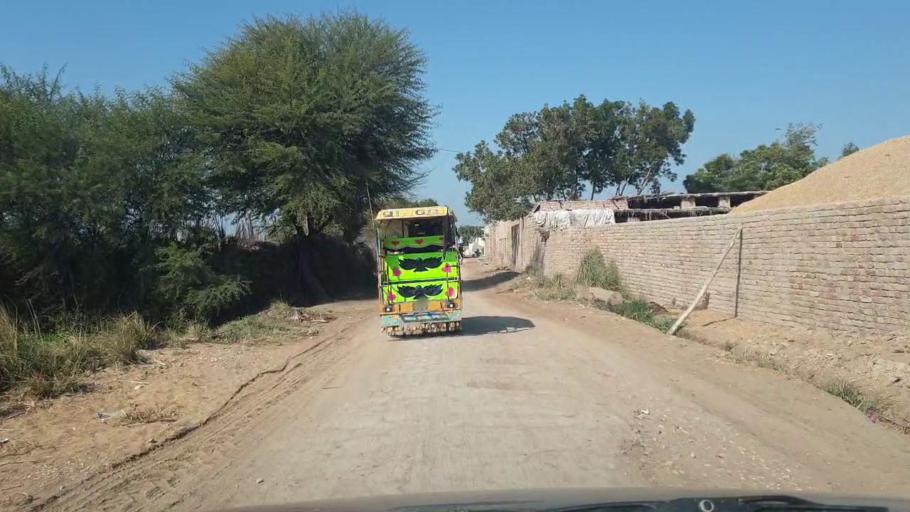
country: PK
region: Sindh
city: Shahdadpur
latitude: 25.8874
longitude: 68.5405
